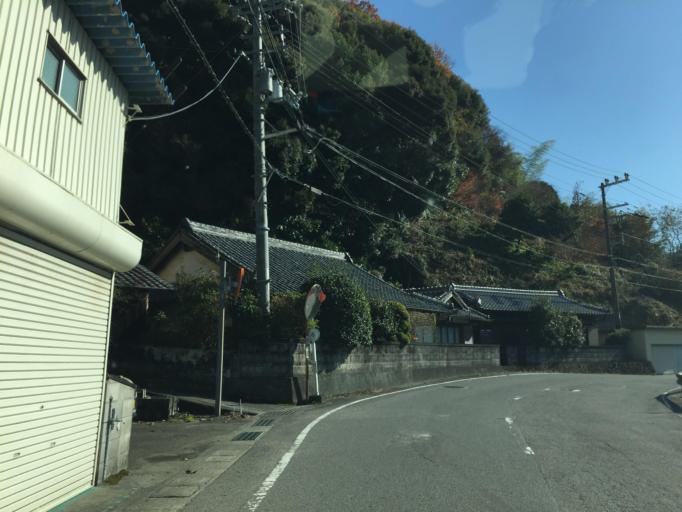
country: JP
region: Wakayama
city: Iwade
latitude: 34.1507
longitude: 135.3721
